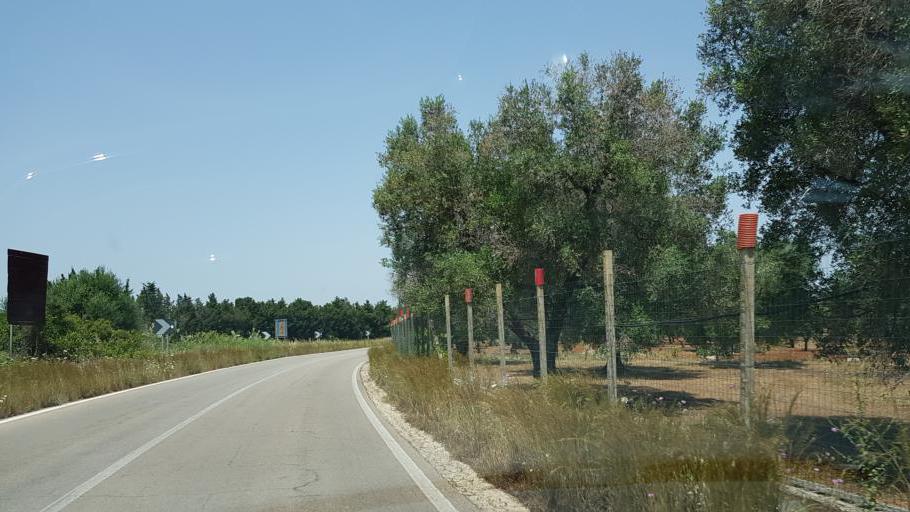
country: IT
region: Apulia
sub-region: Provincia di Lecce
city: Porto Cesareo
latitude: 40.3013
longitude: 17.9179
